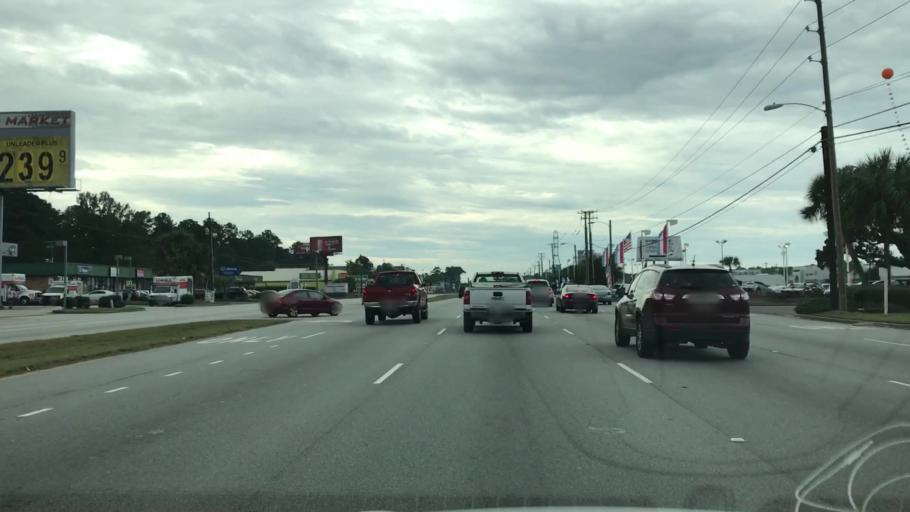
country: US
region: South Carolina
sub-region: Berkeley County
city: Goose Creek
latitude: 32.9612
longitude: -80.0437
